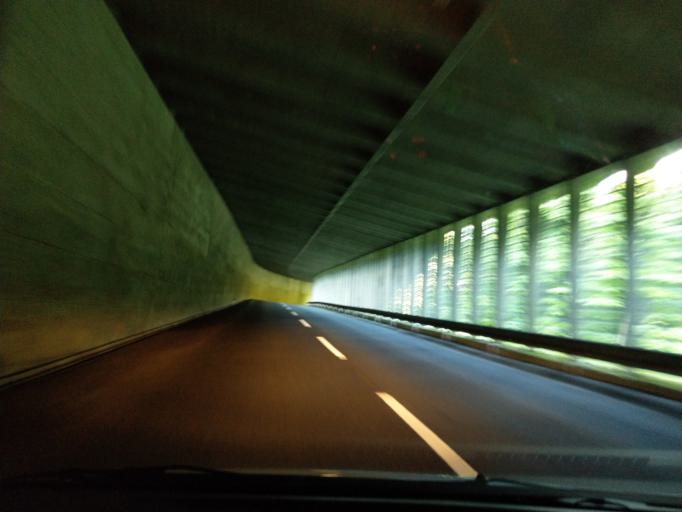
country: JP
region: Akita
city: Kakunodatemachi
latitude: 39.8717
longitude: 140.4843
